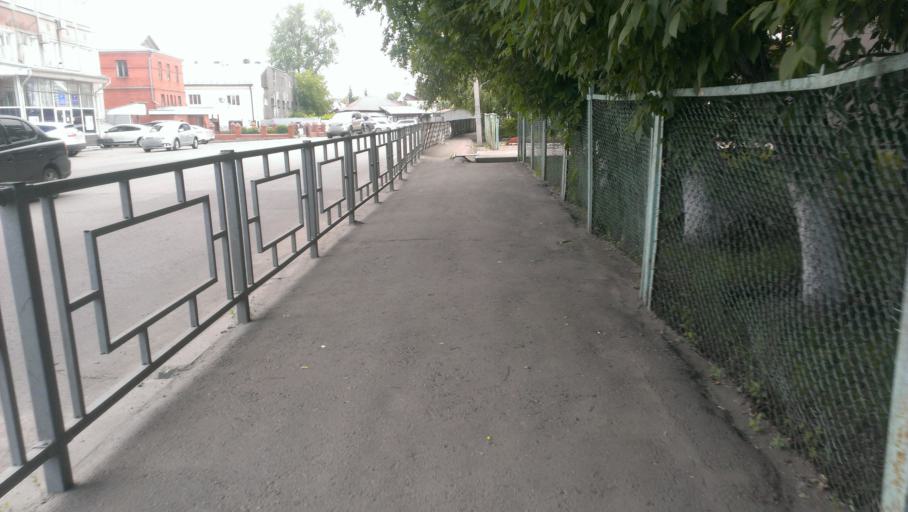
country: RU
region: Altai Krai
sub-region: Gorod Barnaulskiy
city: Barnaul
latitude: 53.3394
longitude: 83.7322
